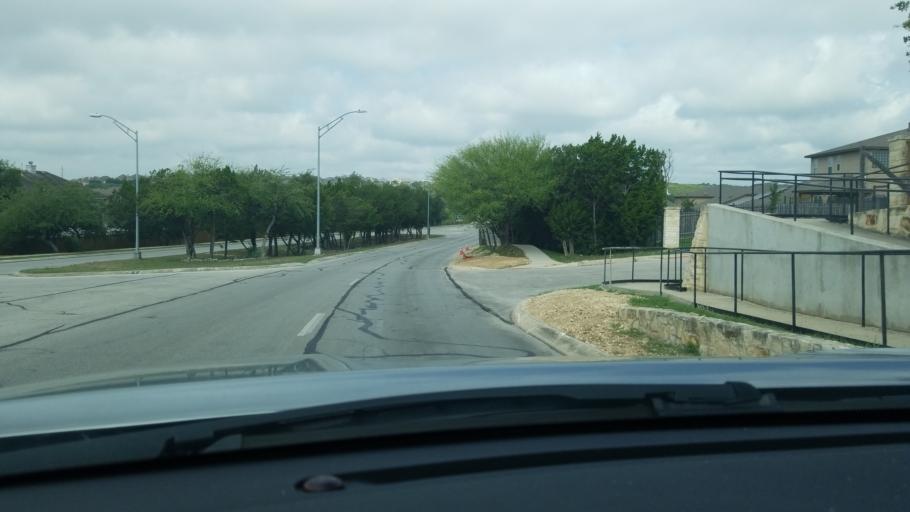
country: US
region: Texas
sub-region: Bexar County
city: Timberwood Park
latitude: 29.6849
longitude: -98.4684
